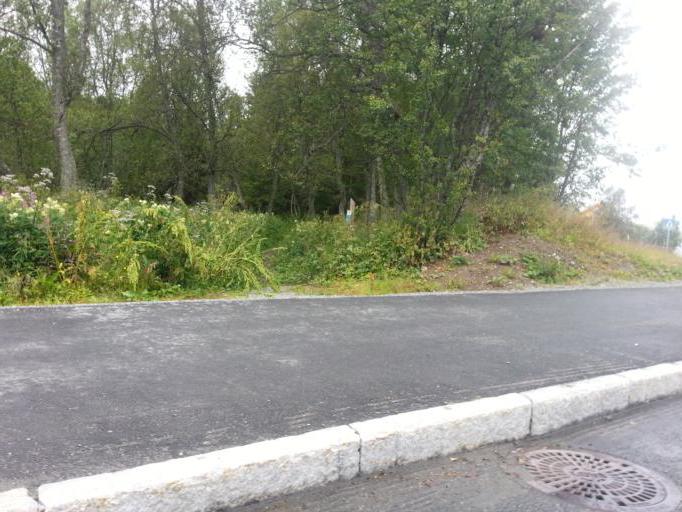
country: NO
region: Troms
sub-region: Tromso
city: Tromso
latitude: 69.6332
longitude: 18.9116
